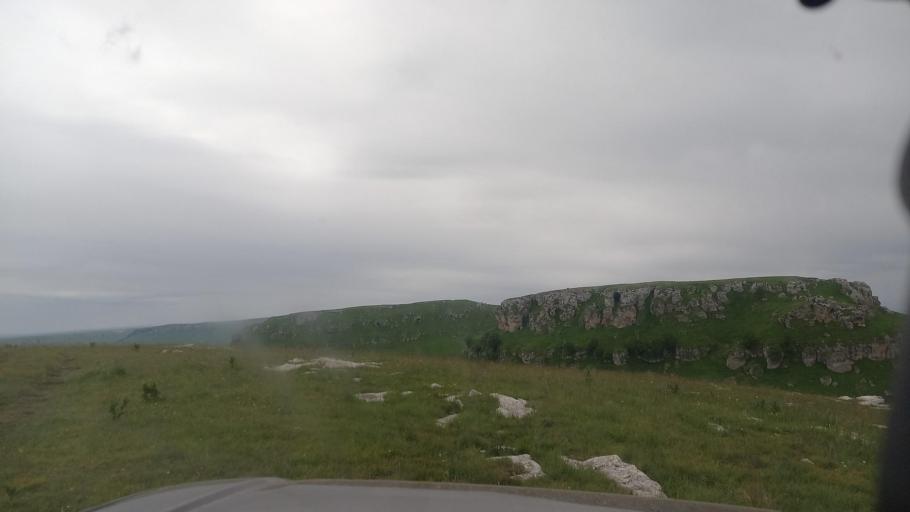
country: RU
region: Karachayevo-Cherkesiya
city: Pregradnaya
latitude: 43.9735
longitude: 41.2915
